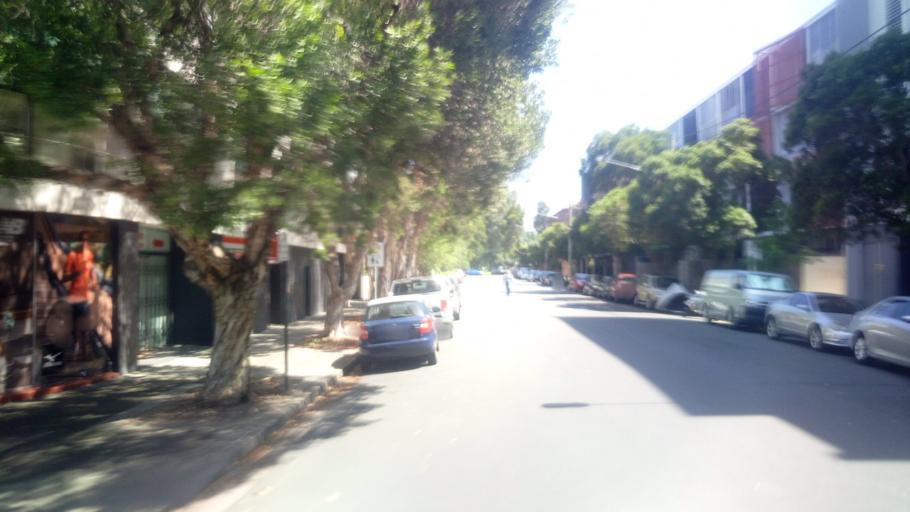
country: AU
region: New South Wales
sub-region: City of Sydney
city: Alexandria
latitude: -33.9019
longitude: 151.1989
